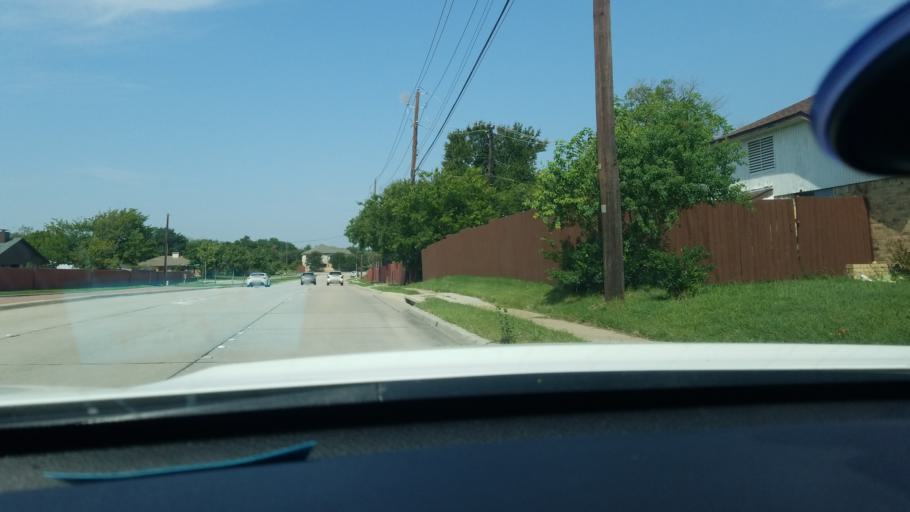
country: US
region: Texas
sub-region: Dallas County
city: Carrollton
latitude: 32.9703
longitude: -96.8676
